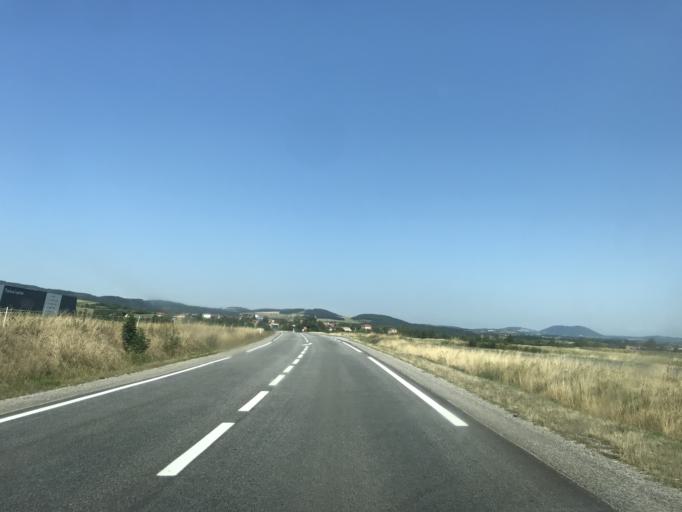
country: FR
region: Auvergne
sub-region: Departement de la Haute-Loire
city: Bains
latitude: 45.0769
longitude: 3.7586
